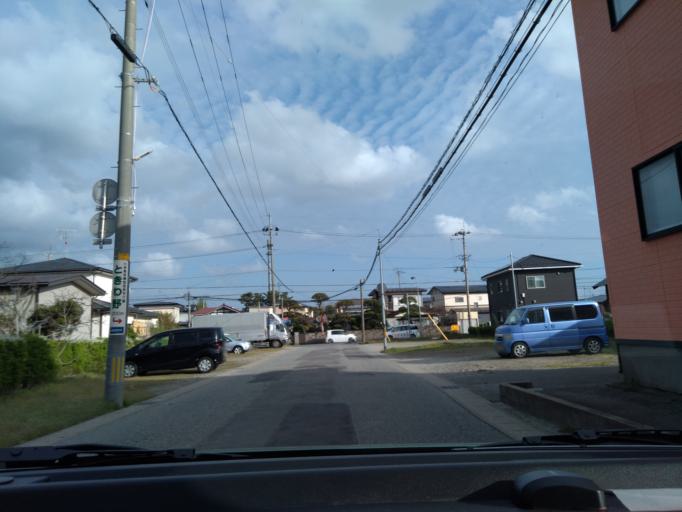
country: JP
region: Akita
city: Akita Shi
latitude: 39.7694
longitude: 140.0828
